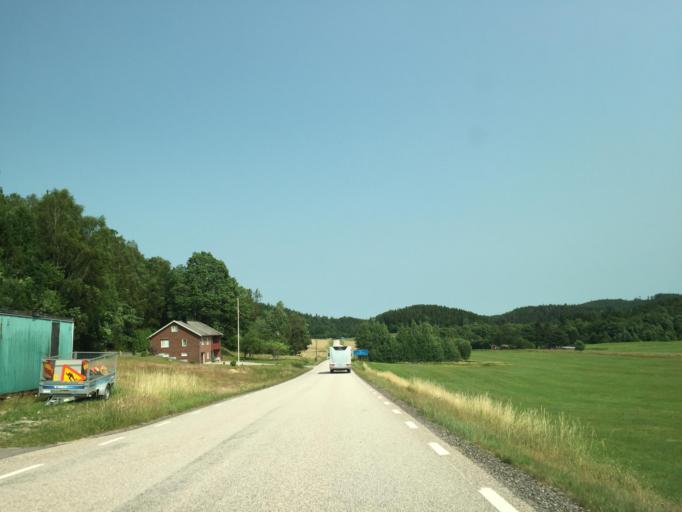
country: SE
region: Vaestra Goetaland
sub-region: Lilla Edets Kommun
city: Lilla Edet
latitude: 58.1503
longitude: 12.0439
